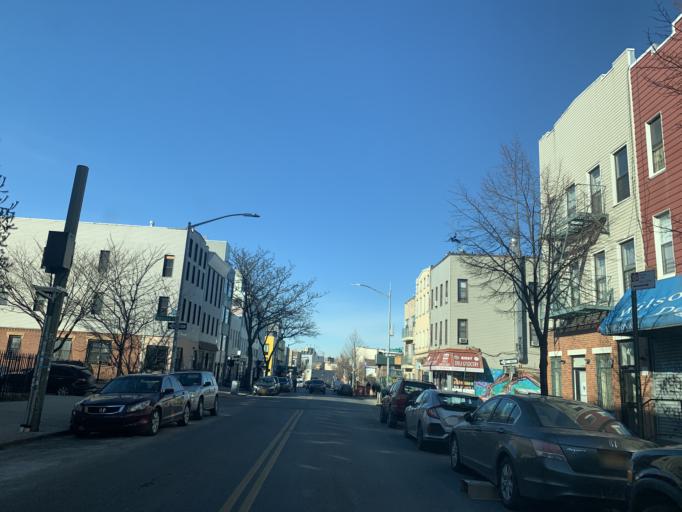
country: US
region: New York
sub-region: Queens County
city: Long Island City
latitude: 40.7025
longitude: -73.9288
